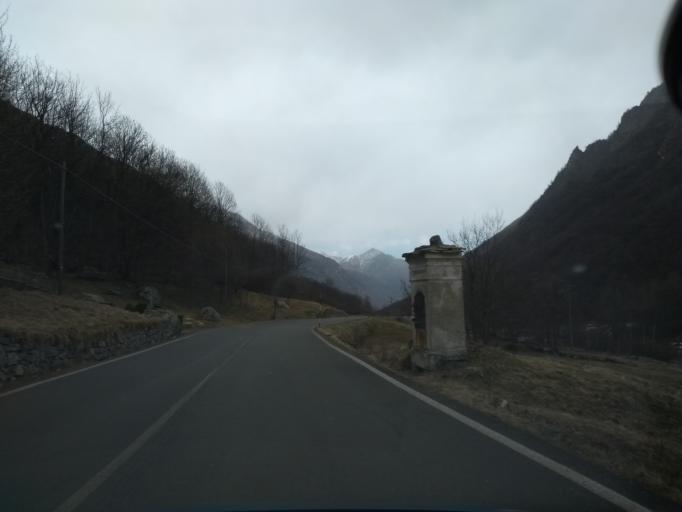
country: IT
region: Piedmont
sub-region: Provincia di Torino
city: Groscavallo
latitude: 45.3654
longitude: 7.2318
